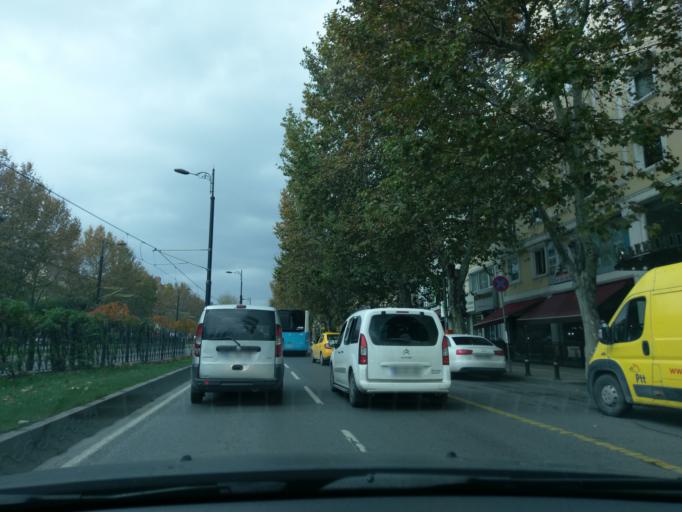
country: TR
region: Istanbul
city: Istanbul
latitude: 41.0133
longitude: 28.9376
